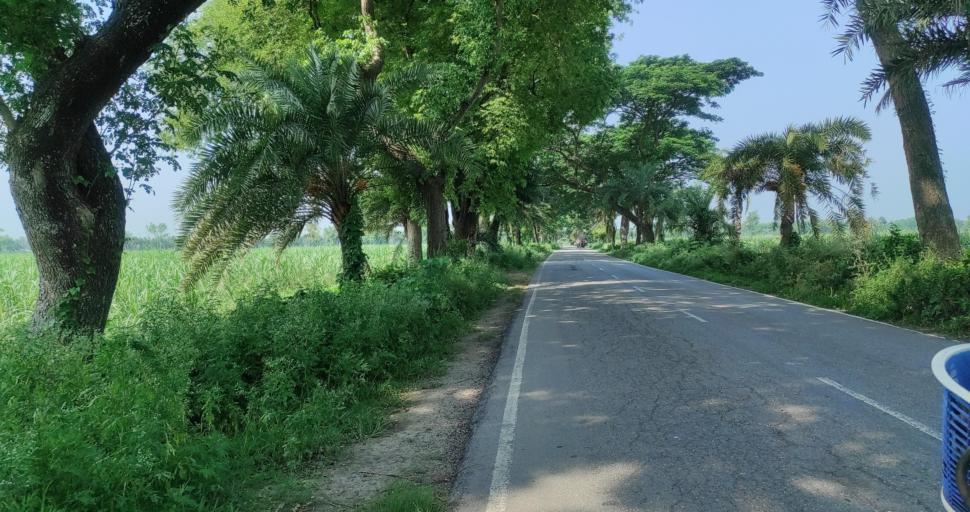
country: BD
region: Rajshahi
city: Ishurdi
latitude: 24.2684
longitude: 89.0530
